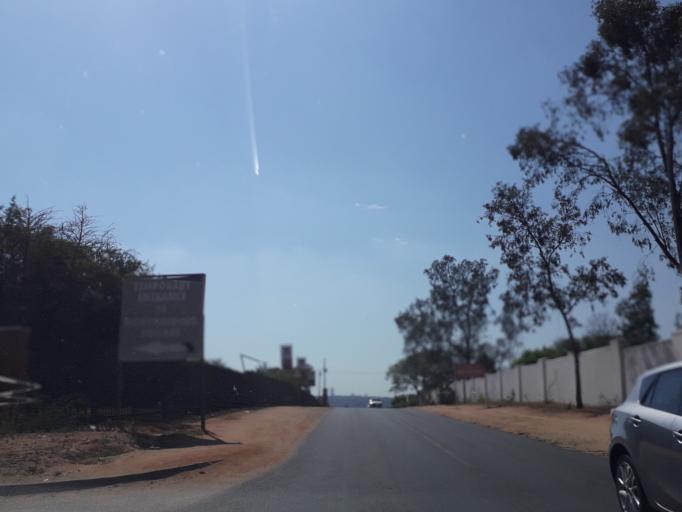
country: ZA
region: Gauteng
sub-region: West Rand District Municipality
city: Muldersdriseloop
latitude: -26.0562
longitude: 27.9650
